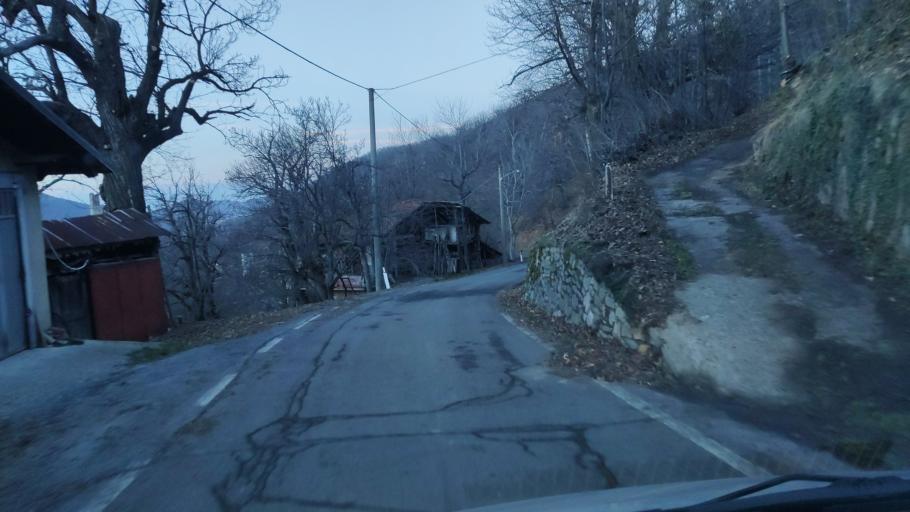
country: IT
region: Piedmont
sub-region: Provincia di Cuneo
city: Lisio
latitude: 44.2899
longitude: 7.9829
